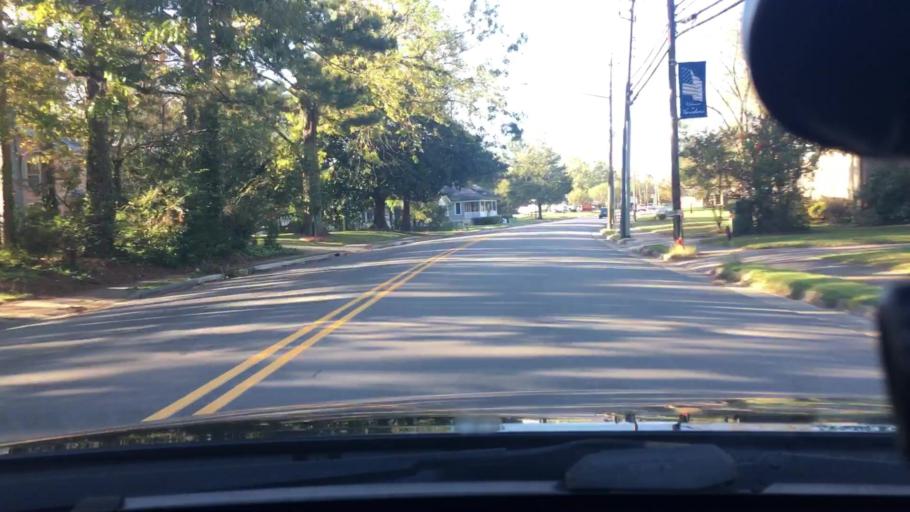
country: US
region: North Carolina
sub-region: Craven County
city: Vanceboro
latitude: 35.3015
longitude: -77.1540
